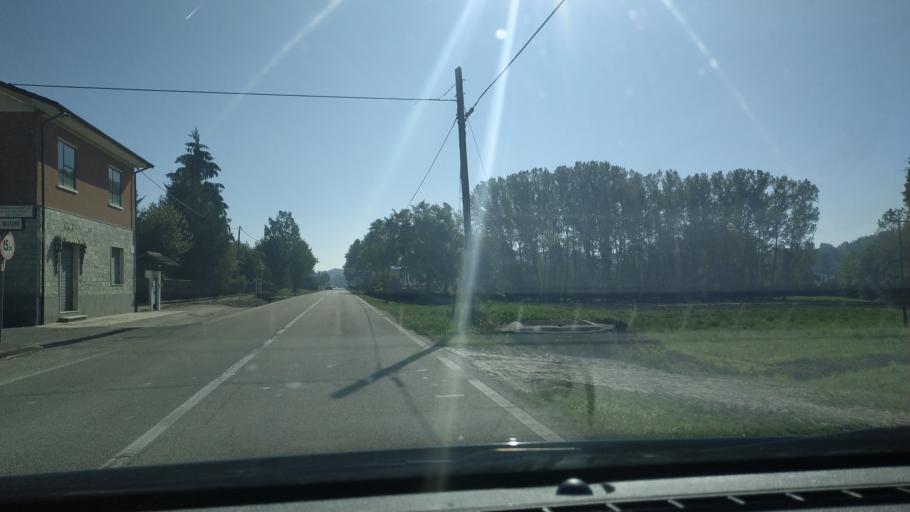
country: IT
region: Piedmont
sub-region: Provincia di Asti
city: Robella
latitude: 45.0890
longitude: 8.1001
